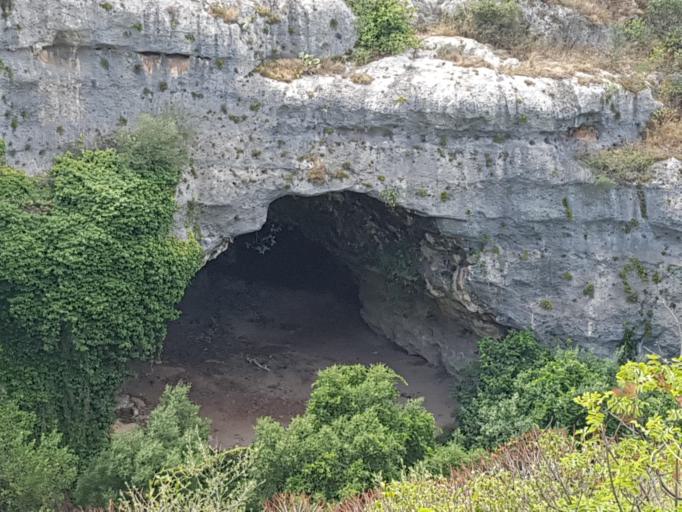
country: IT
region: Sicily
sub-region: Provincia di Siracusa
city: Sortino
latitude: 37.1564
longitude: 15.0278
